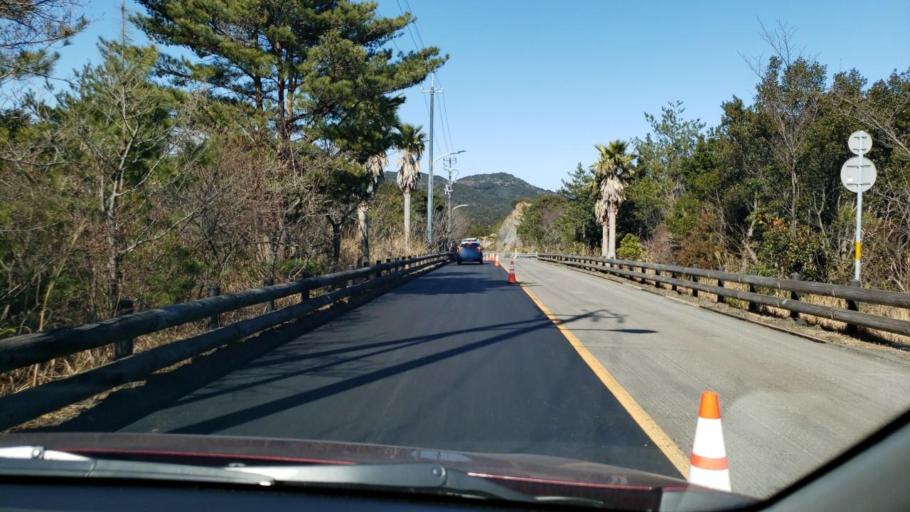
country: JP
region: Tokushima
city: Narutocho-mitsuishi
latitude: 34.2298
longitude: 134.6190
